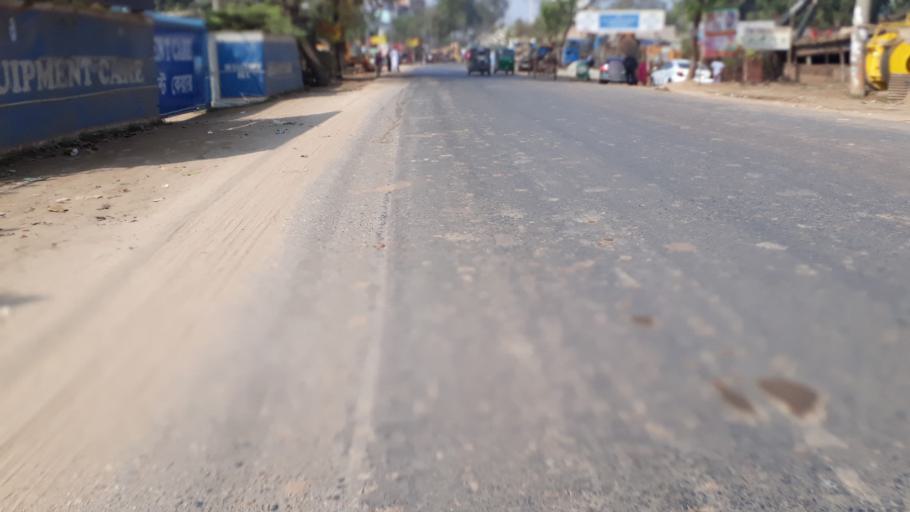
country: BD
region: Dhaka
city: Tungi
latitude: 23.9028
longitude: 90.3257
